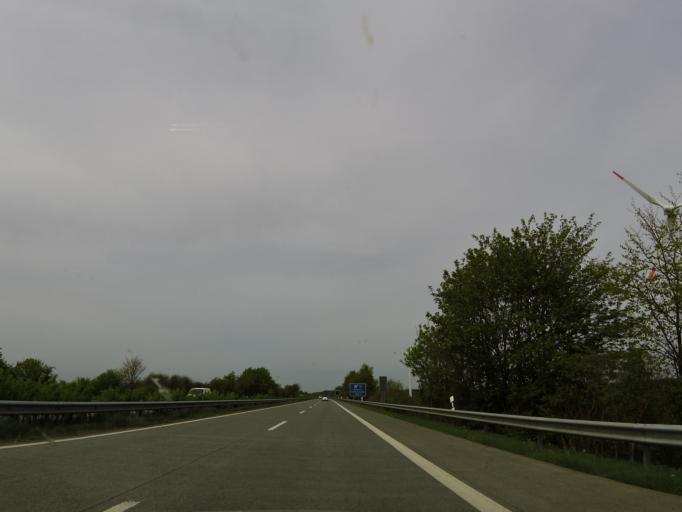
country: DE
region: Schleswig-Holstein
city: Bokelrehm
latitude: 54.0530
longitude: 9.3844
